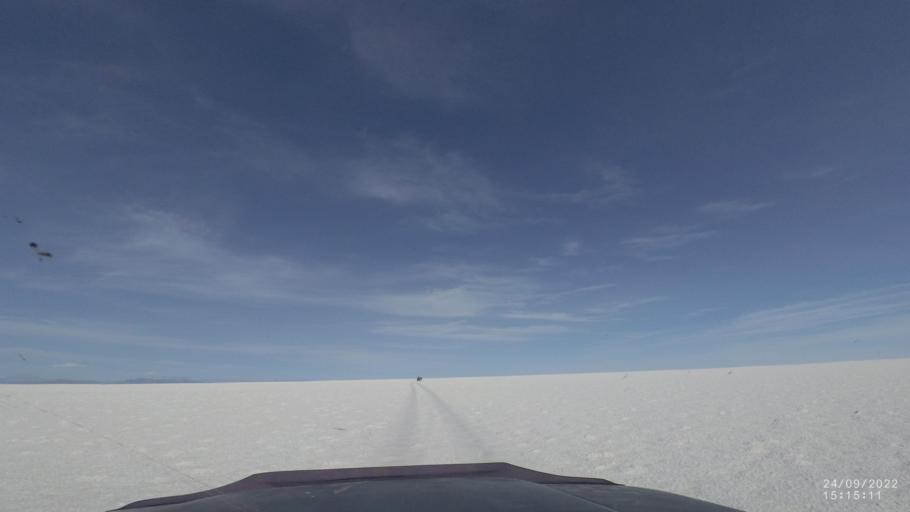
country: BO
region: Potosi
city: Colchani
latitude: -19.9709
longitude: -67.4479
